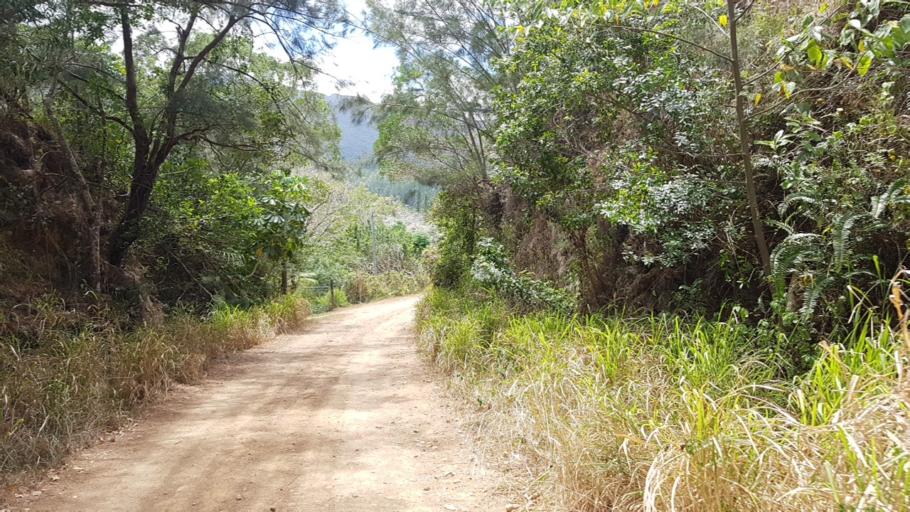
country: NC
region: South Province
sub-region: Dumbea
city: Dumbea
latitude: -22.1806
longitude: 166.4811
